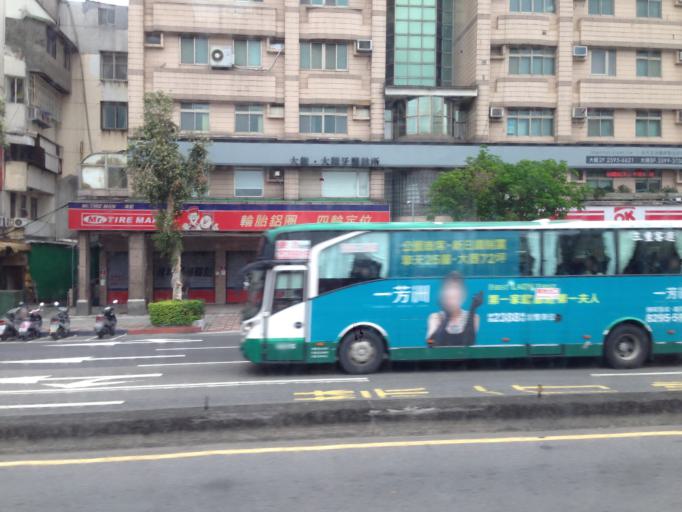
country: TW
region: Taipei
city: Taipei
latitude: 25.0727
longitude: 121.5139
